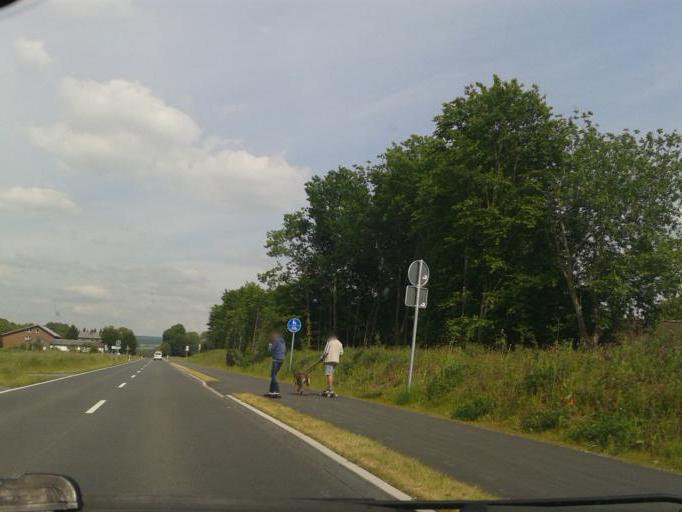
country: DE
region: North Rhine-Westphalia
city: Bad Lippspringe
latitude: 51.7707
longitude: 8.8127
